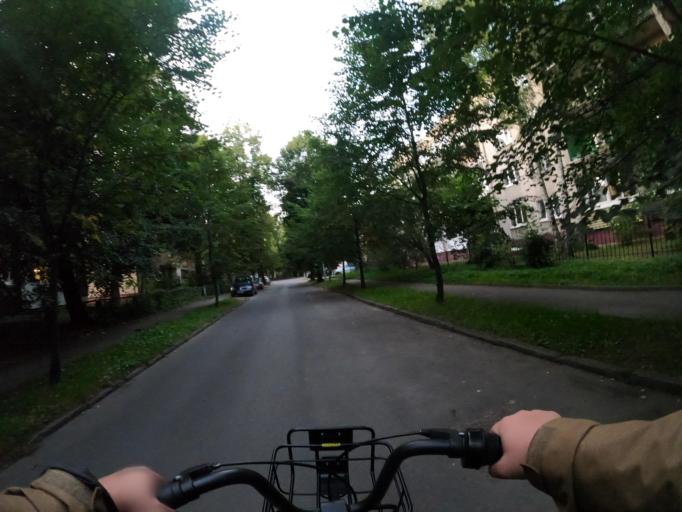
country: RU
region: Kaliningrad
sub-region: Gorod Kaliningrad
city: Kaliningrad
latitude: 54.7261
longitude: 20.4765
